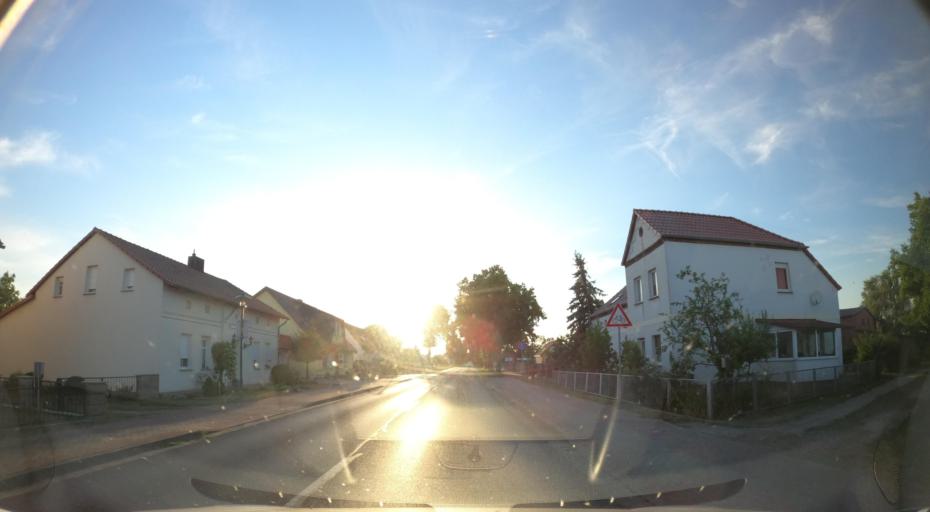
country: DE
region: Brandenburg
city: Brussow
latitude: 53.4559
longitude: 14.1974
